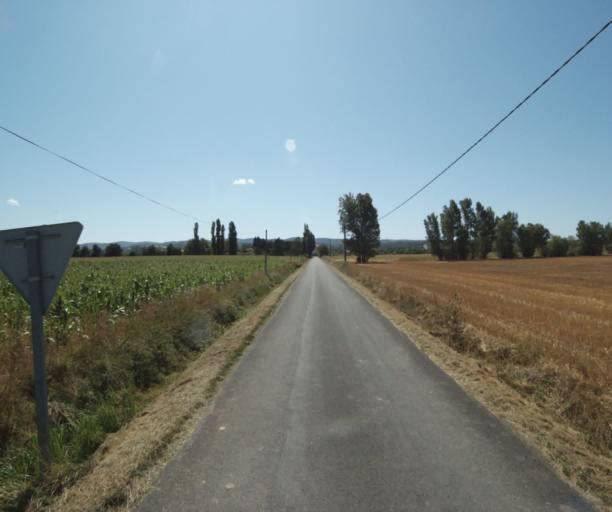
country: FR
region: Midi-Pyrenees
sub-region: Departement de la Haute-Garonne
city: Revel
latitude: 43.4616
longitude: 1.9700
